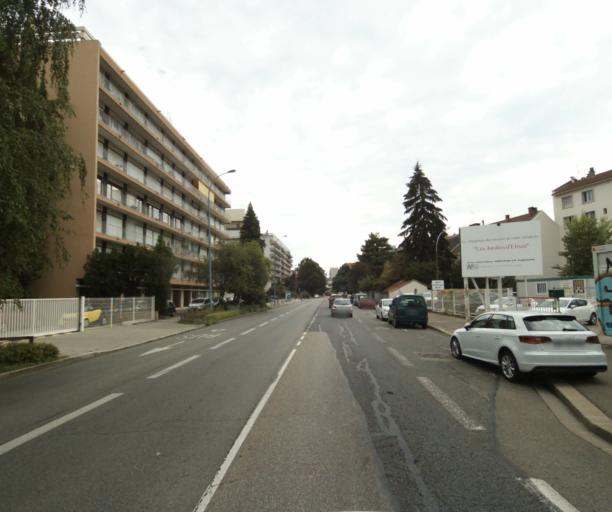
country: FR
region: Rhone-Alpes
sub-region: Departement de l'Isere
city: Grenoble
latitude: 45.1791
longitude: 5.7281
